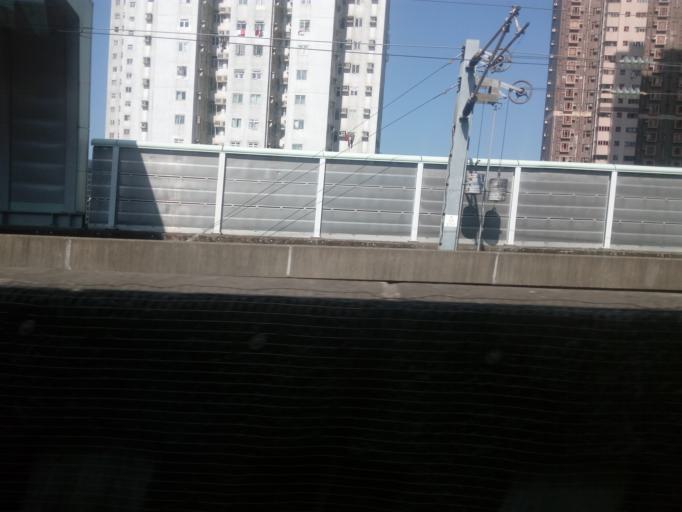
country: HK
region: Sai Kung
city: Sai Kung
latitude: 22.4242
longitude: 114.2293
